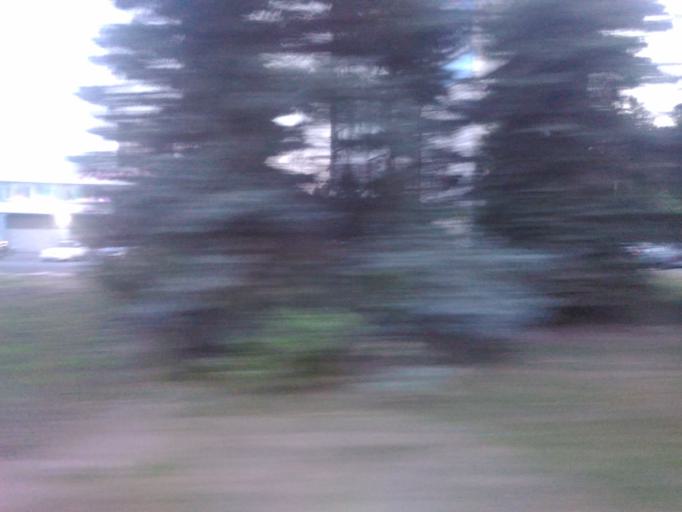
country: RU
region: Ulyanovsk
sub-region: Ulyanovskiy Rayon
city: Ulyanovsk
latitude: 54.3068
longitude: 48.3482
